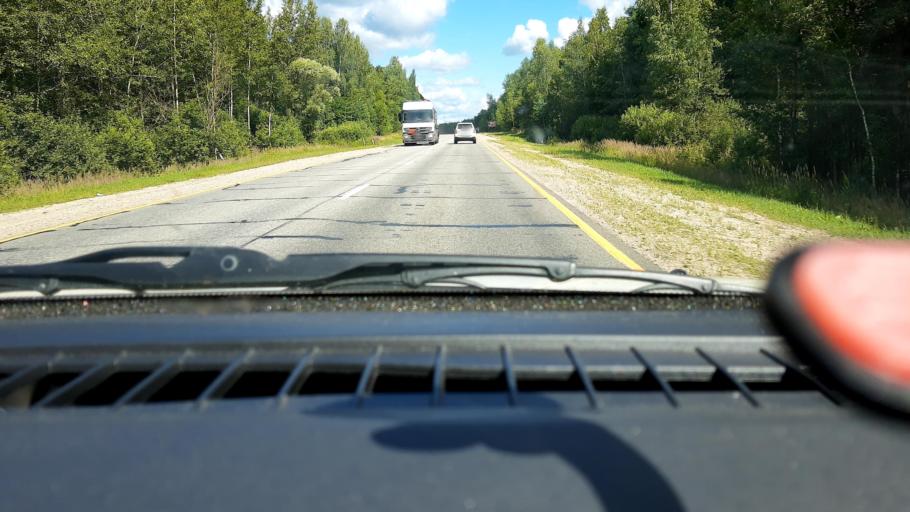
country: RU
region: Nizjnij Novgorod
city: Arzamas
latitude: 55.4090
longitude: 43.9150
